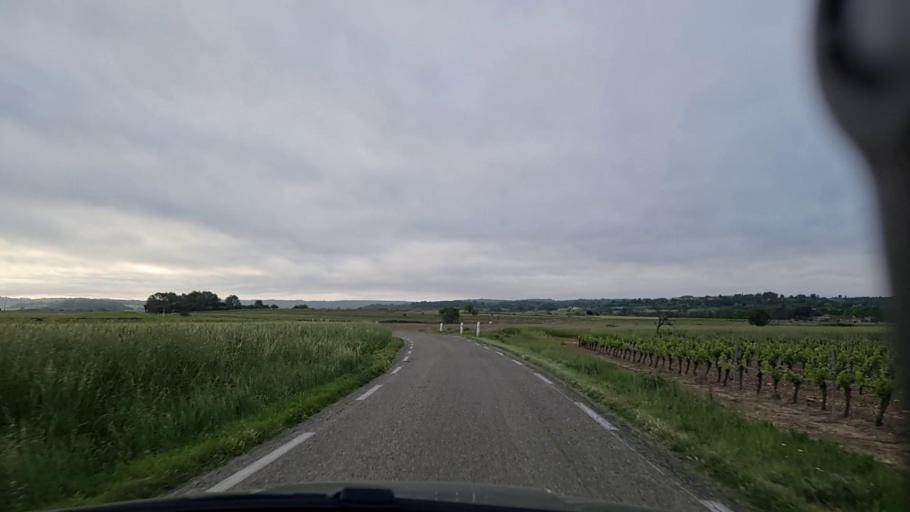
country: FR
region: Languedoc-Roussillon
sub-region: Departement du Gard
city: Villevieille
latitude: 43.8276
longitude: 4.1072
